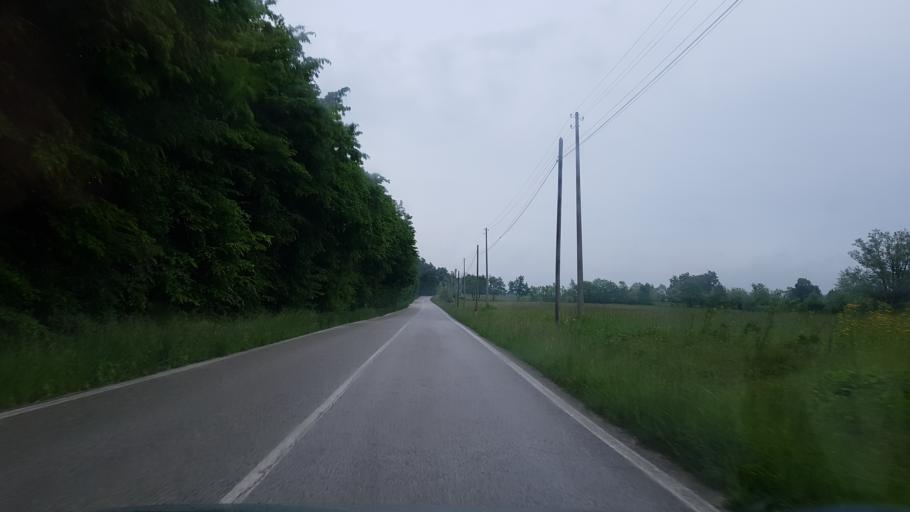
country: IT
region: Friuli Venezia Giulia
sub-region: Provincia di Udine
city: Corno di Rosazzo
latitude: 45.9881
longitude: 13.4207
